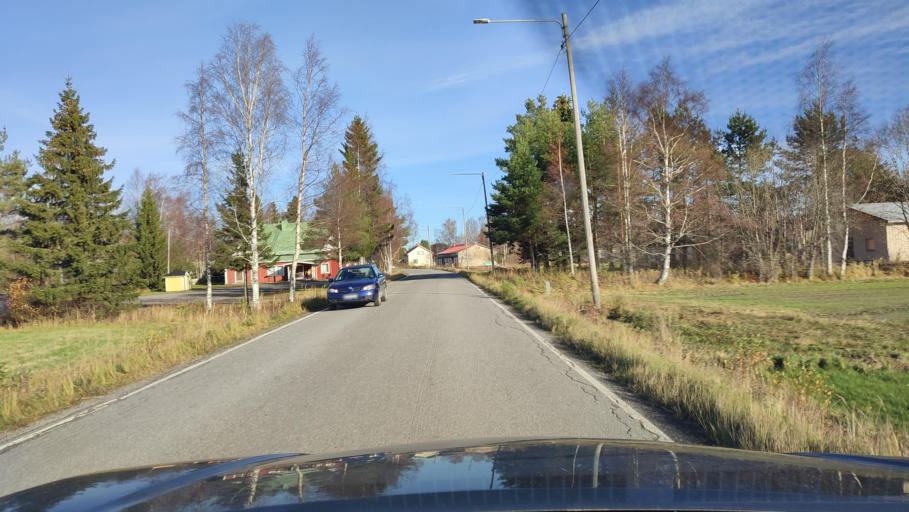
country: FI
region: Southern Ostrobothnia
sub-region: Suupohja
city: Teuva
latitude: 62.4521
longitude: 21.6018
